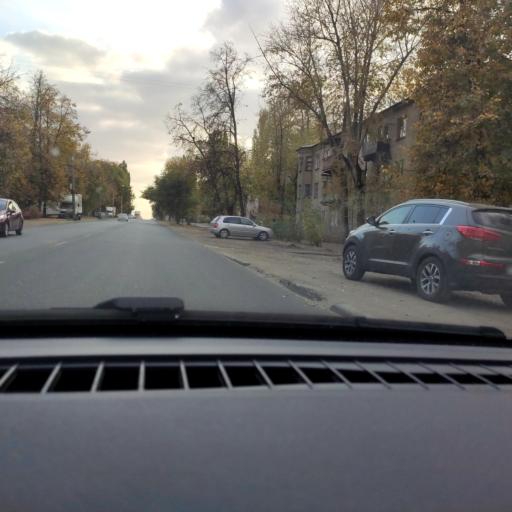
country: RU
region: Voronezj
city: Voronezh
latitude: 51.6775
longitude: 39.1581
